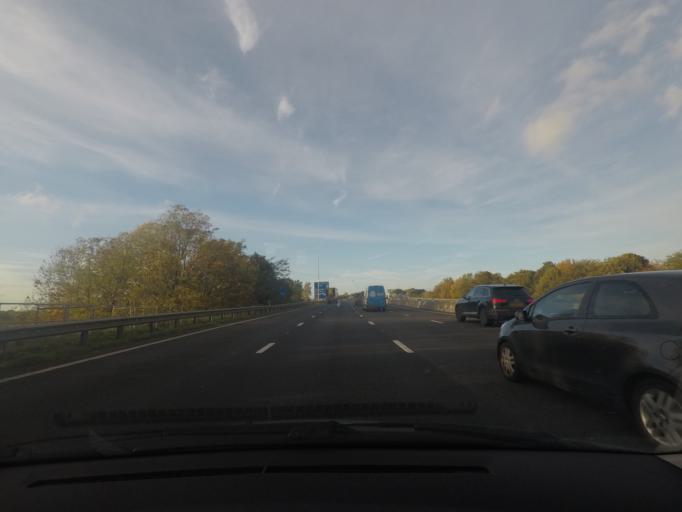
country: GB
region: England
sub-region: City and Borough of Wakefield
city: Horbury
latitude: 53.6771
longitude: -1.5534
